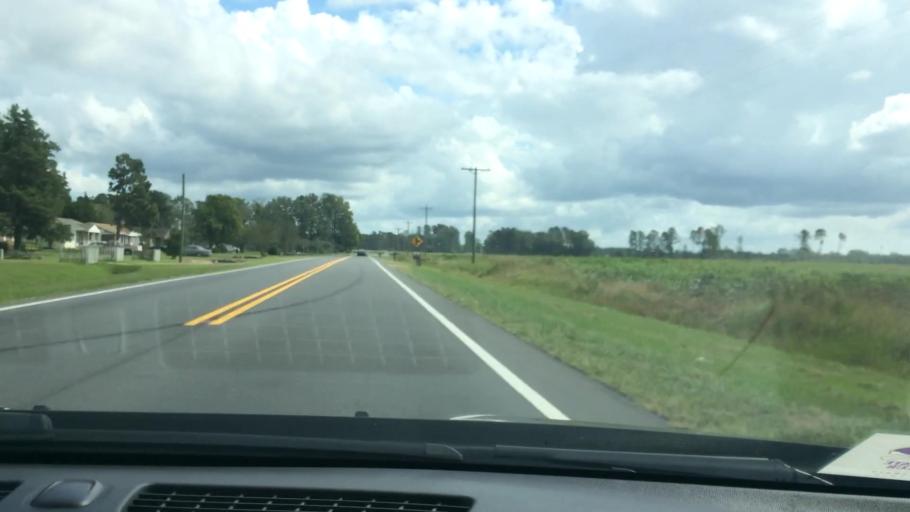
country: US
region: North Carolina
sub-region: Pitt County
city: Farmville
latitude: 35.5705
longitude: -77.5730
